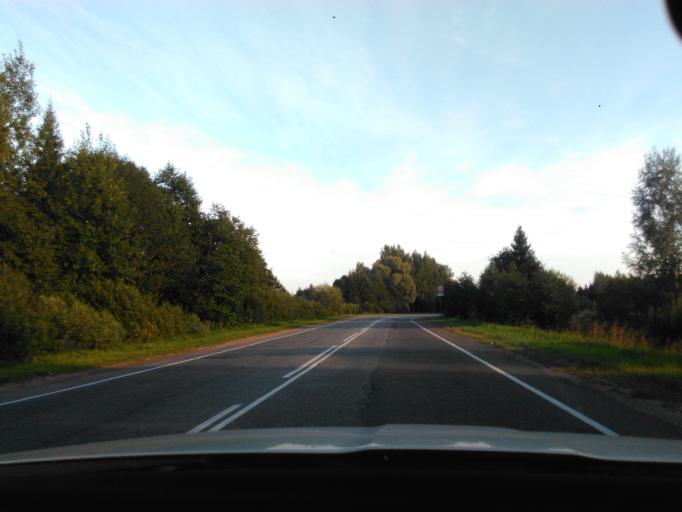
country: RU
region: Tverskaya
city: Konakovo
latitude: 56.6440
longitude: 36.7090
